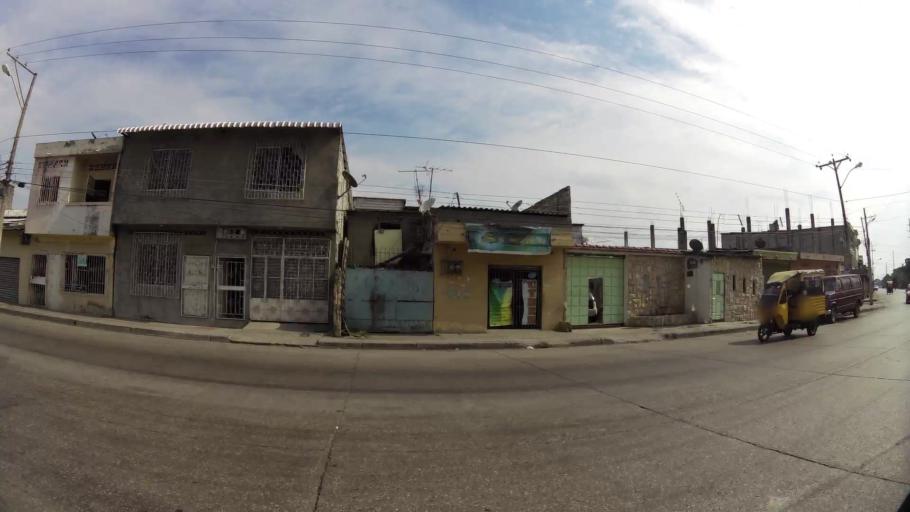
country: EC
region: Guayas
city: Guayaquil
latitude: -2.2554
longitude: -79.9000
